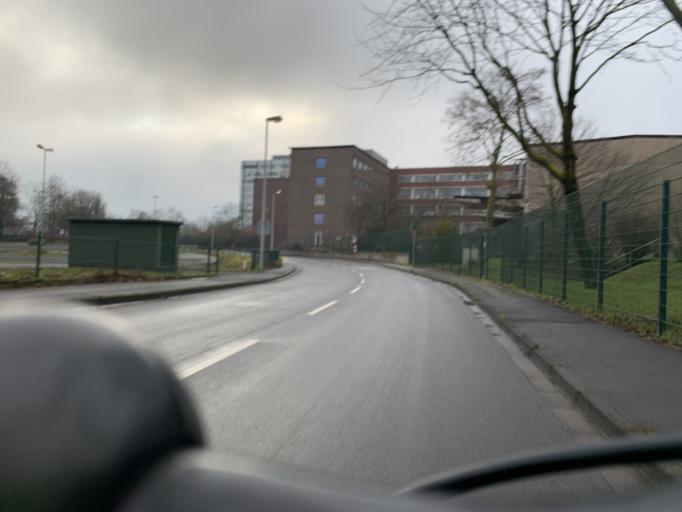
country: DE
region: North Rhine-Westphalia
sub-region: Regierungsbezirk Dusseldorf
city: Krefeld
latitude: 51.3720
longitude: 6.6650
